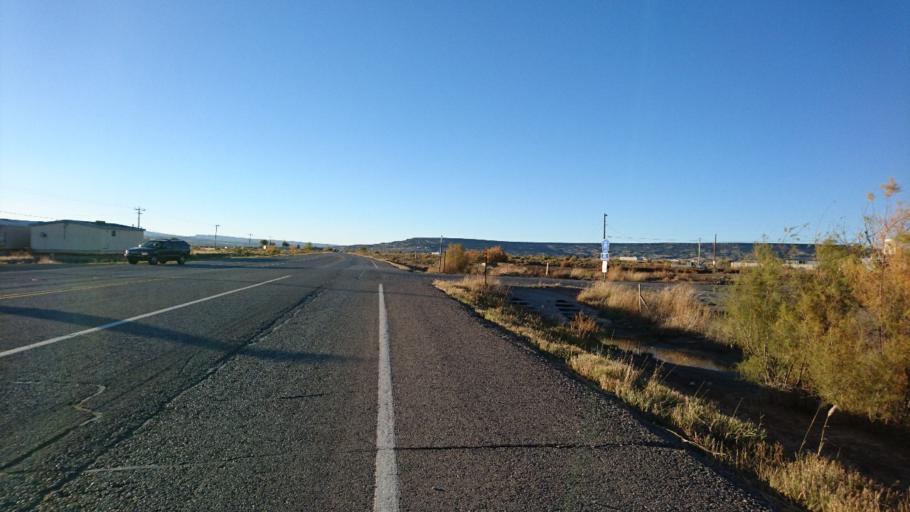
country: US
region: New Mexico
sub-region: Cibola County
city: Grants
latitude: 35.1306
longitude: -107.8104
